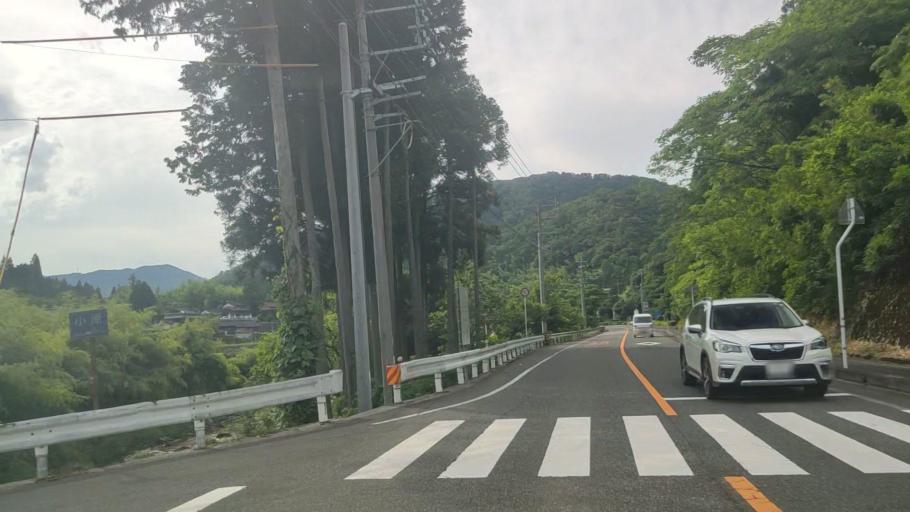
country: JP
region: Tottori
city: Tottori
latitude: 35.3398
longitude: 134.1795
